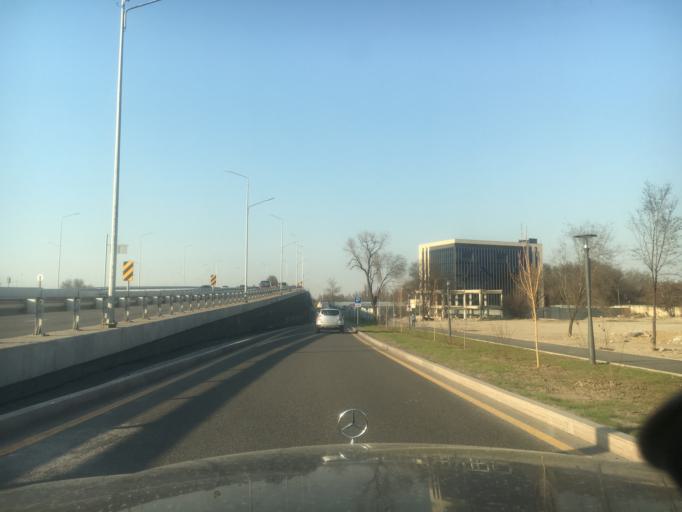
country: KZ
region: Almaty Qalasy
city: Almaty
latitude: 43.2730
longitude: 76.9449
